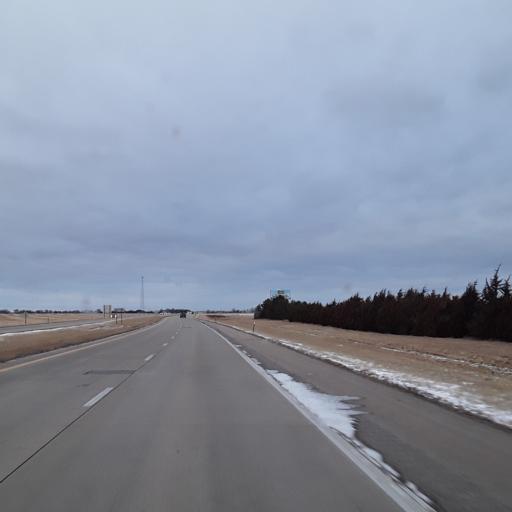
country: US
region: Nebraska
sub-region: Fillmore County
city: Geneva
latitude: 40.6413
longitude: -97.5956
